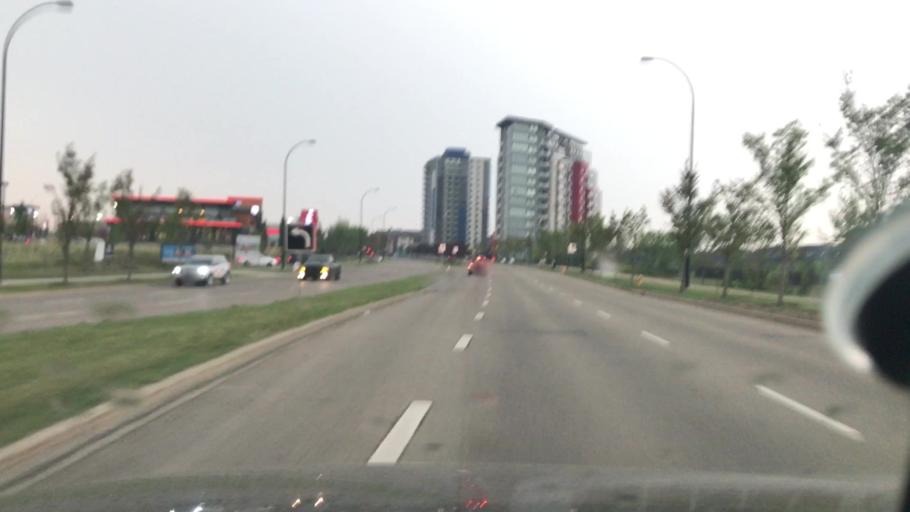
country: CA
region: Alberta
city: Devon
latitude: 53.4346
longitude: -113.6054
